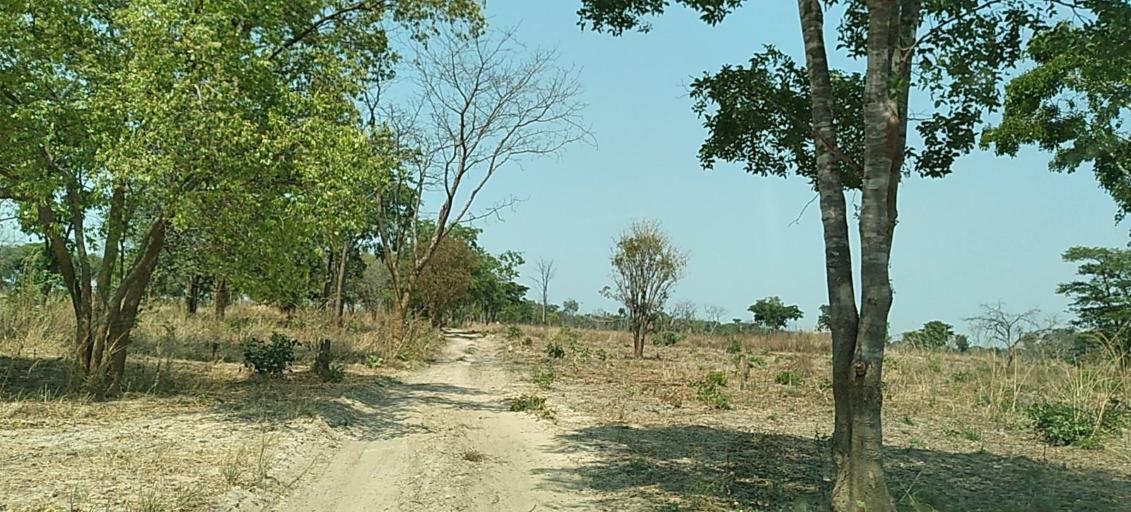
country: ZM
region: Copperbelt
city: Mpongwe
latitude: -13.8680
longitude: 28.0532
